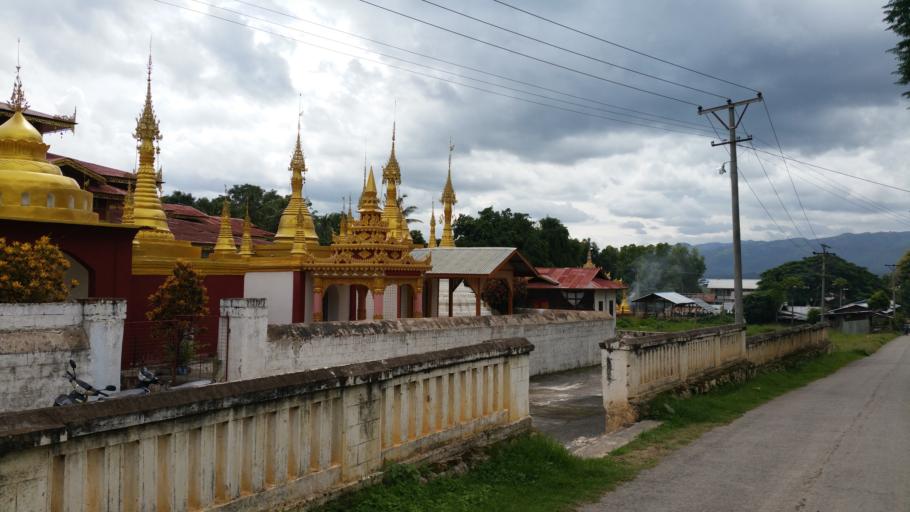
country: MM
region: Shan
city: Taunggyi
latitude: 20.5796
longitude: 96.9443
